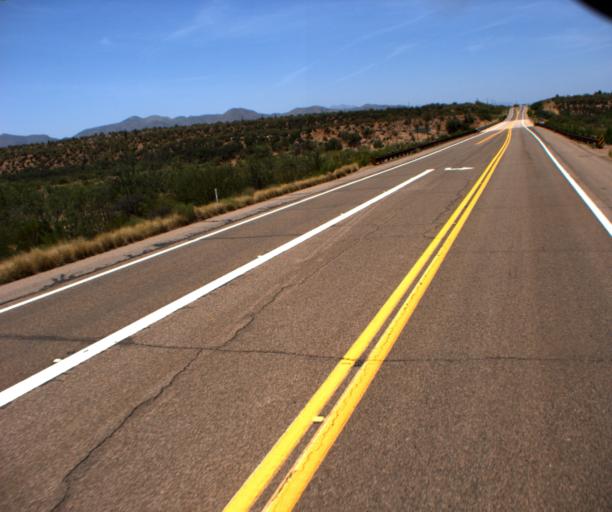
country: US
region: Arizona
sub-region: Gila County
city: Miami
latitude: 33.5972
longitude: -110.9981
